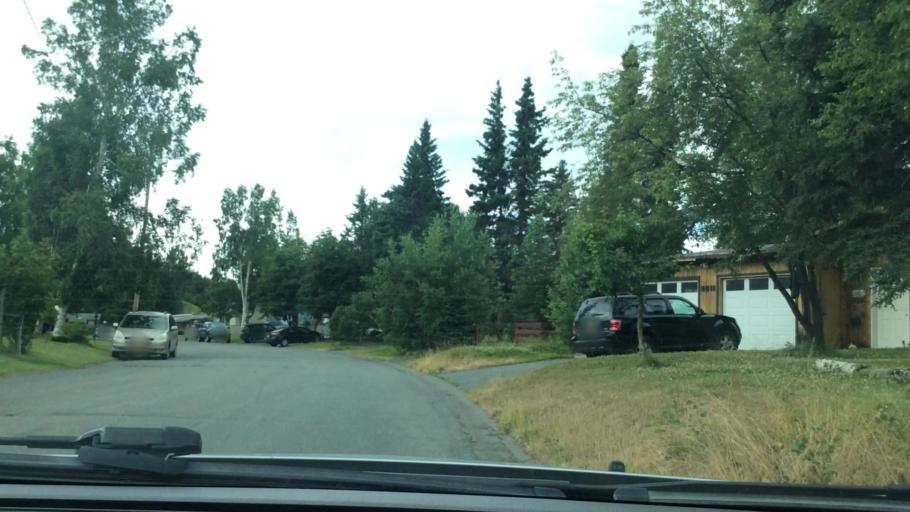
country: US
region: Alaska
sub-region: Anchorage Municipality
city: Anchorage
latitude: 61.2019
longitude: -149.7717
